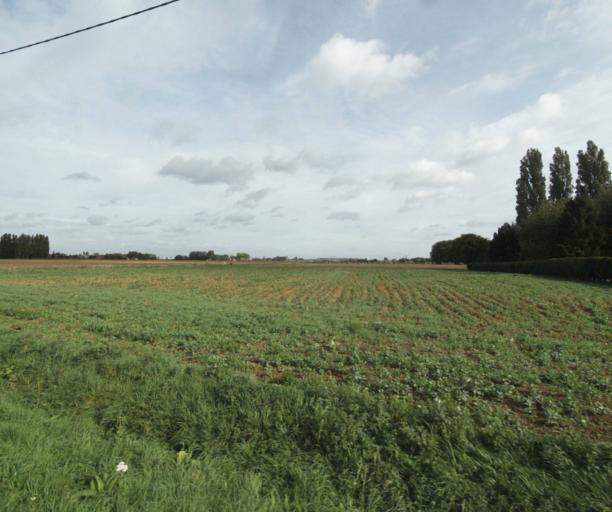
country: FR
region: Nord-Pas-de-Calais
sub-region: Departement du Nord
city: Bois-Grenier
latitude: 50.6314
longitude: 2.8712
